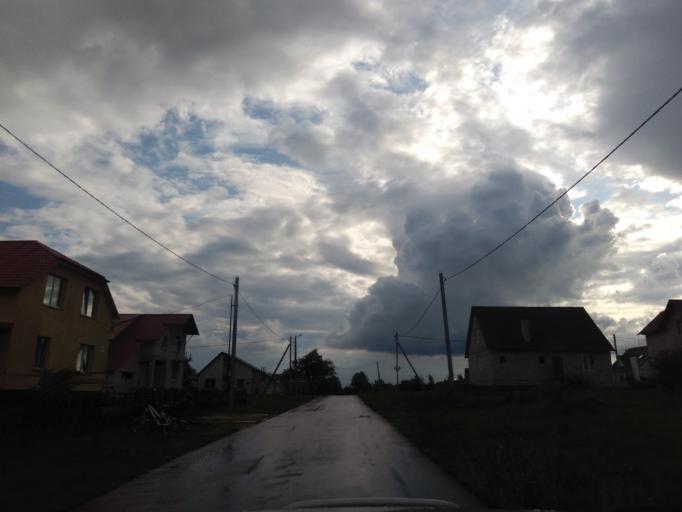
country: BY
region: Minsk
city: Kapyl'
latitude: 53.1649
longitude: 27.0910
